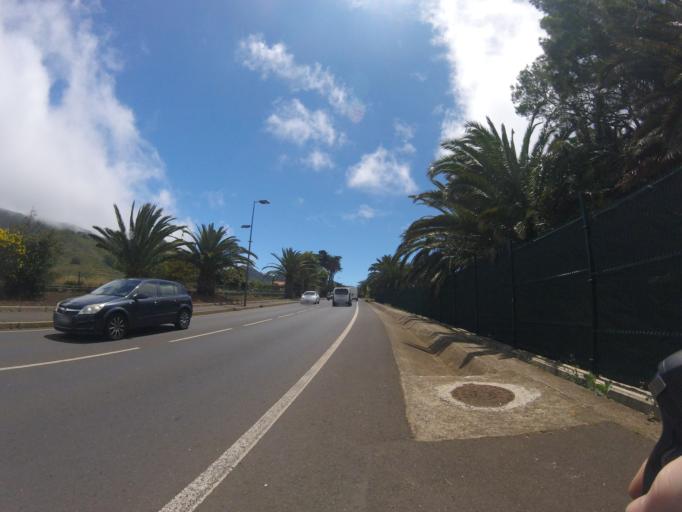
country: ES
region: Canary Islands
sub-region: Provincia de Santa Cruz de Tenerife
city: Tegueste
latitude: 28.5192
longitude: -16.3332
